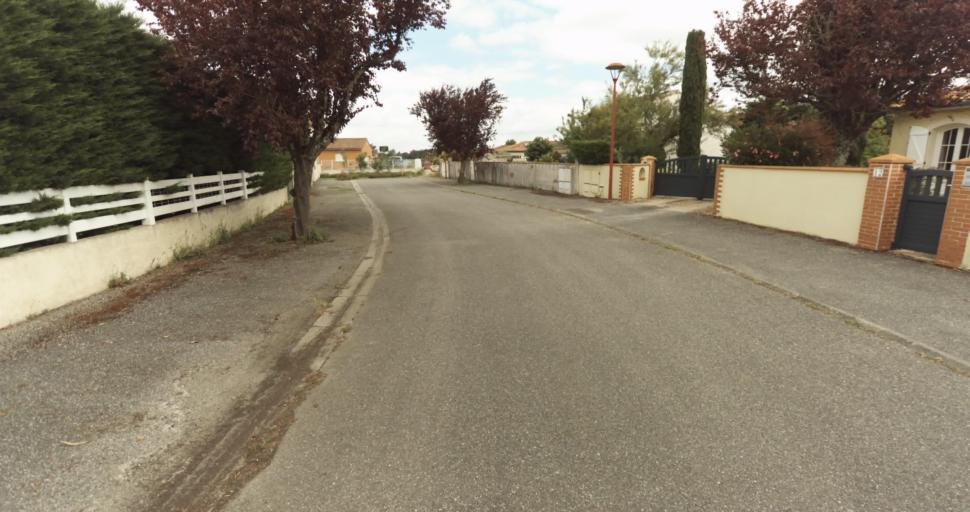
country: FR
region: Midi-Pyrenees
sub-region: Departement de la Haute-Garonne
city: Fontenilles
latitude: 43.5552
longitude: 1.1961
